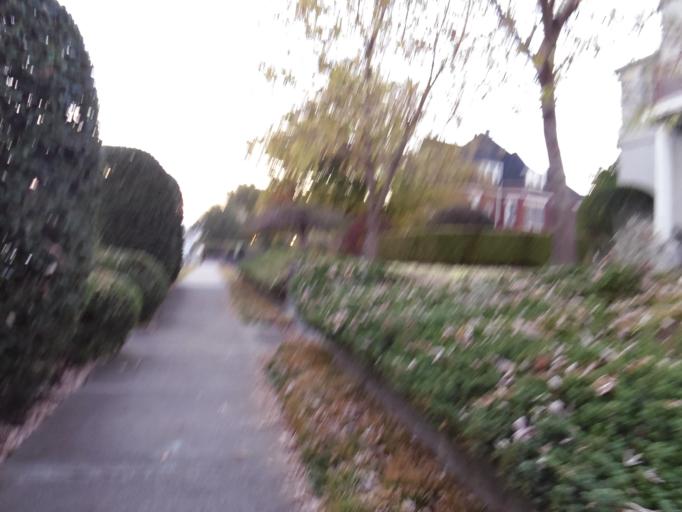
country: US
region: Tennessee
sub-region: Knox County
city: Knoxville
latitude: 35.9607
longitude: -83.9289
